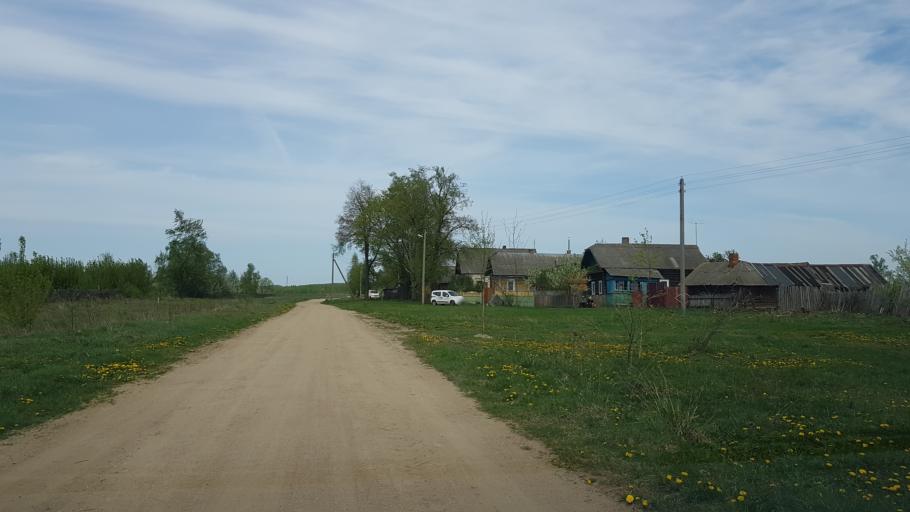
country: BY
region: Mogilev
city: Kirawsk
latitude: 53.2645
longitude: 29.3498
